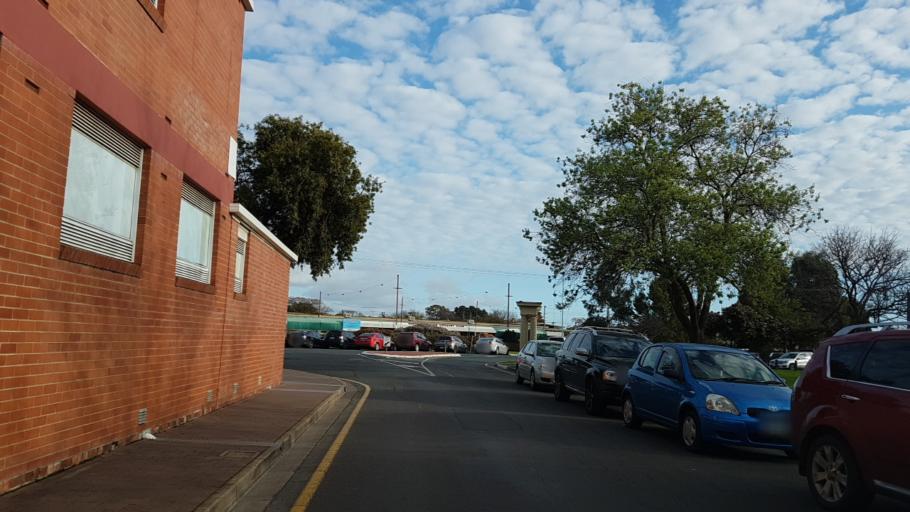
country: AU
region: South Australia
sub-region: Prospect
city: Prospect
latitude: -34.8855
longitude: 138.5999
